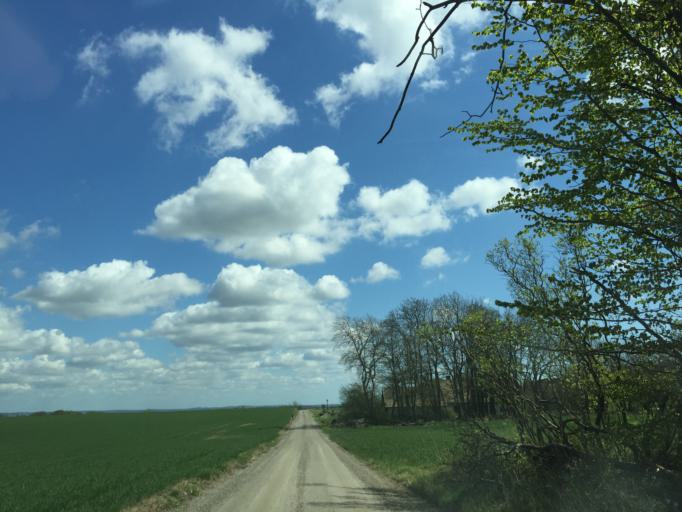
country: SE
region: Skane
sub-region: Lunds Kommun
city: Genarp
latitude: 55.7063
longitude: 13.3554
